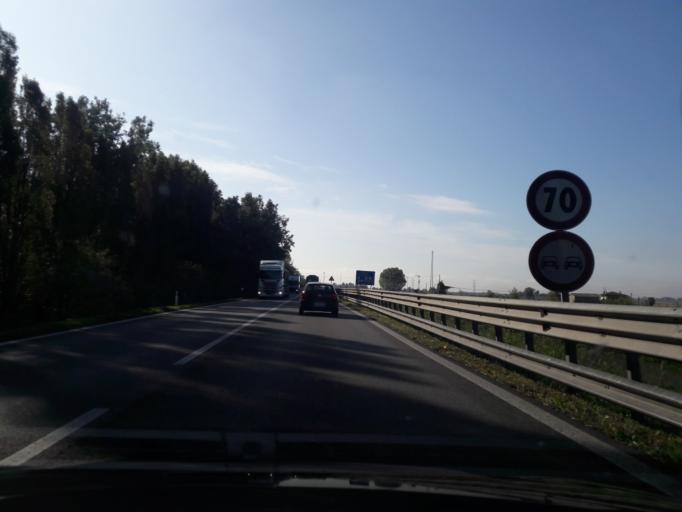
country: IT
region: Veneto
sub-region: Provincia di Padova
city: Codevigo
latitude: 45.2925
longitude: 12.1306
